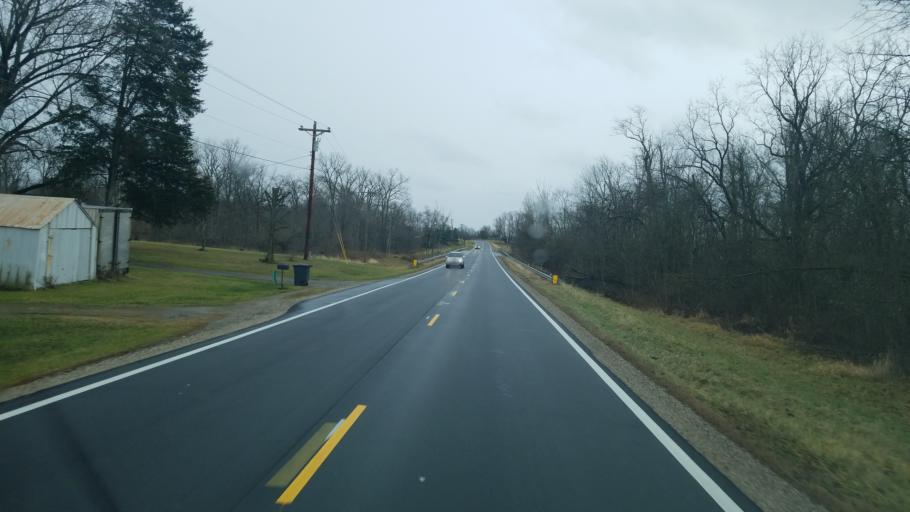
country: US
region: Ohio
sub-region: Union County
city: Richwood
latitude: 40.3771
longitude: -83.4050
